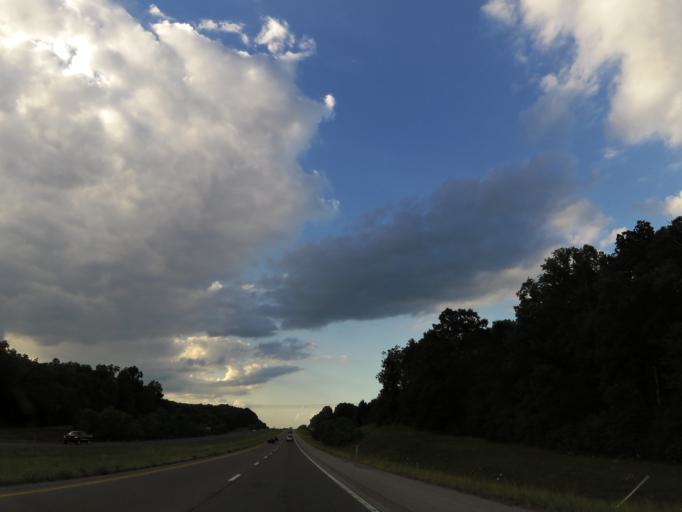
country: US
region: Tennessee
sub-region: Maury County
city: Spring Hill
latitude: 35.6490
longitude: -86.8932
